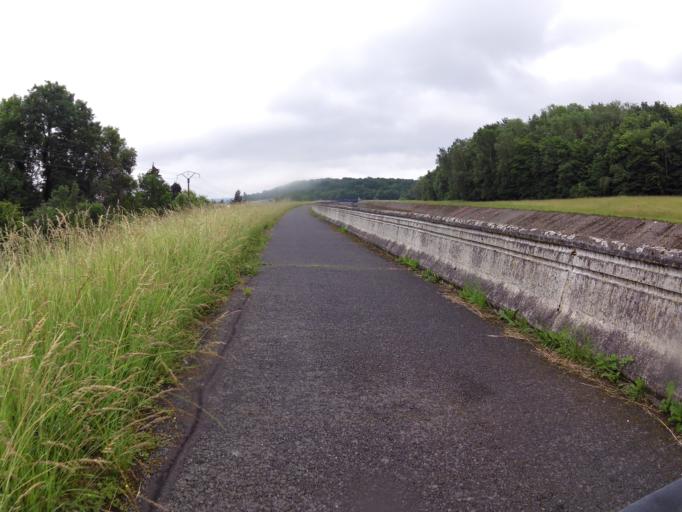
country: FR
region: Champagne-Ardenne
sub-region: Departement de la Haute-Marne
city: Saint-Dizier
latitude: 48.6156
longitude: 4.9084
